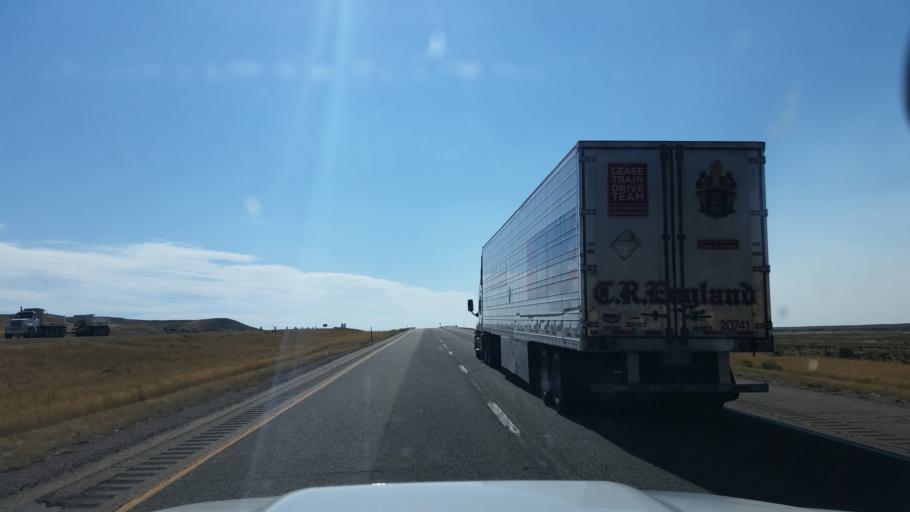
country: US
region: Wyoming
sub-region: Uinta County
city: Lyman
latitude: 41.3869
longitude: -110.2127
